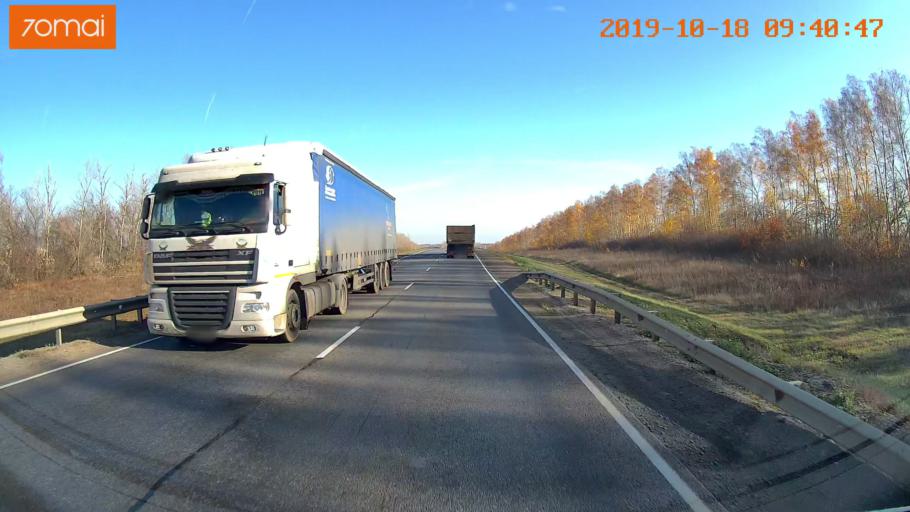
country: RU
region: Tula
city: Kazachka
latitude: 53.2680
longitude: 38.1530
